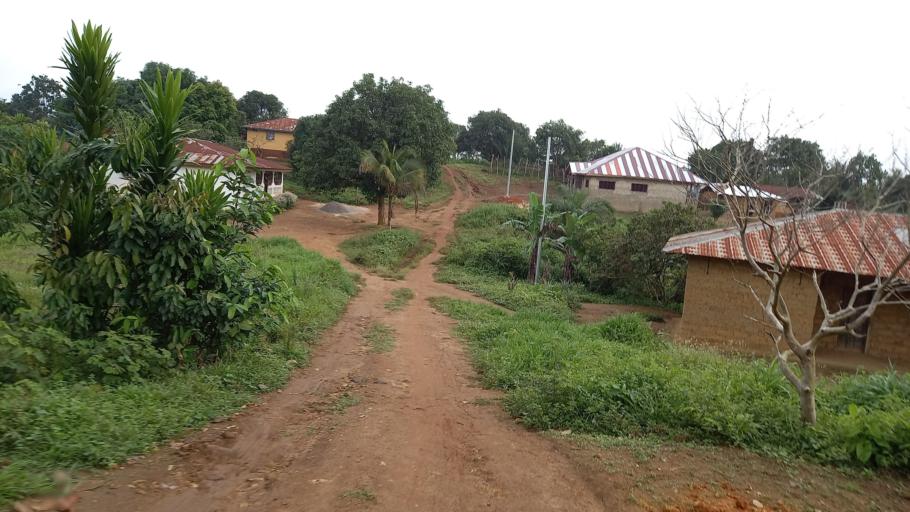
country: SL
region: Eastern Province
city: Kailahun
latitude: 8.2770
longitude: -10.5841
